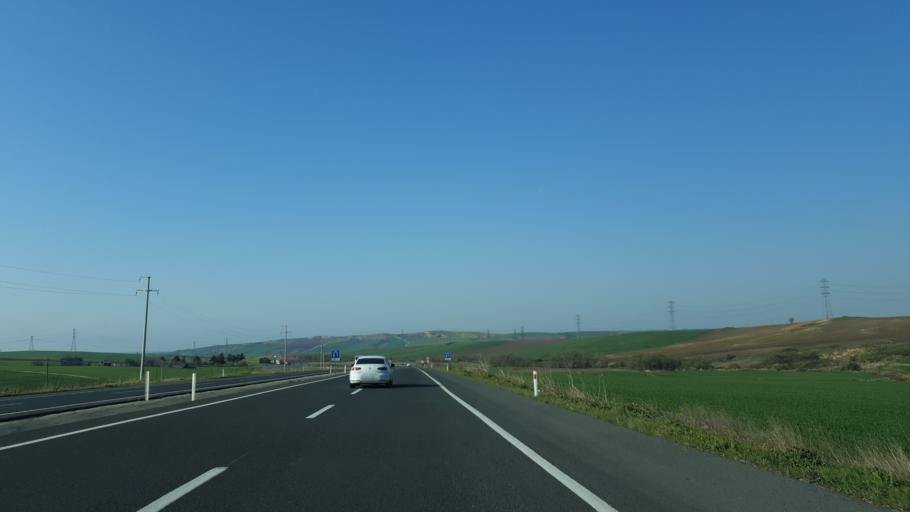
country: TR
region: Tekirdag
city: Corlu
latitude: 41.0893
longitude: 27.7456
